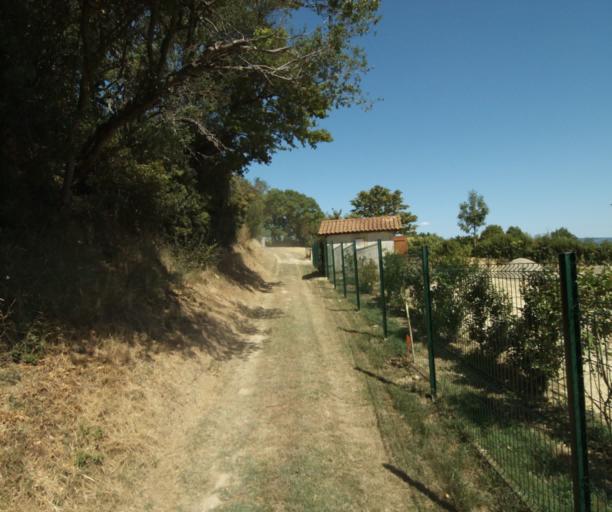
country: FR
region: Midi-Pyrenees
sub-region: Departement de la Haute-Garonne
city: Saint-Felix-Lauragais
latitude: 43.4877
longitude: 1.8992
